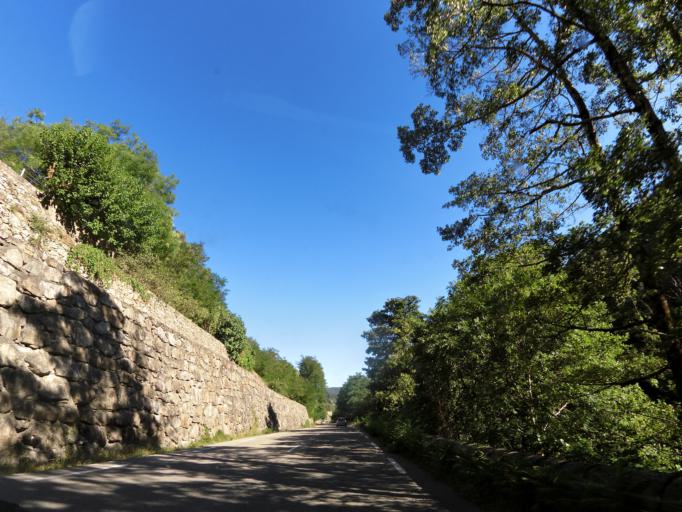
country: FR
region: Languedoc-Roussillon
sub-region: Departement du Gard
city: Valleraugue
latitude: 44.0677
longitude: 3.6781
